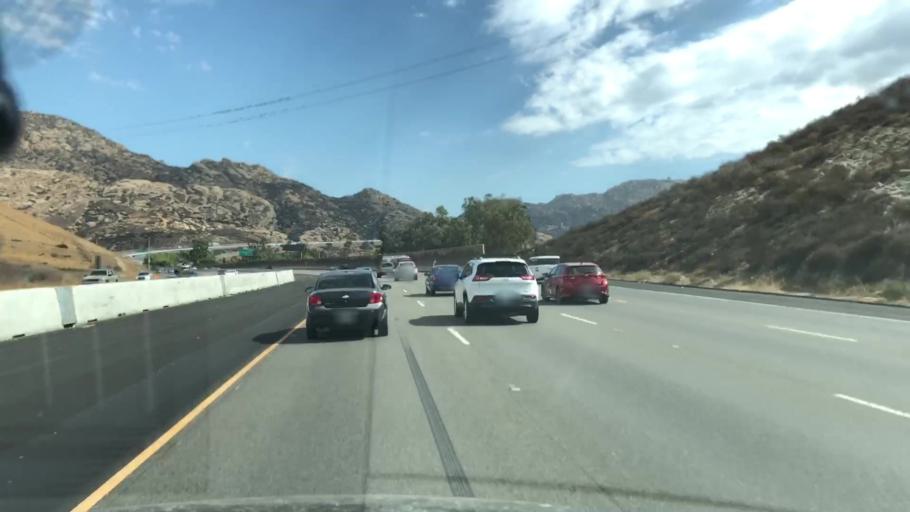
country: US
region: California
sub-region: Ventura County
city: Santa Susana
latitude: 34.2801
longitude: -118.6694
